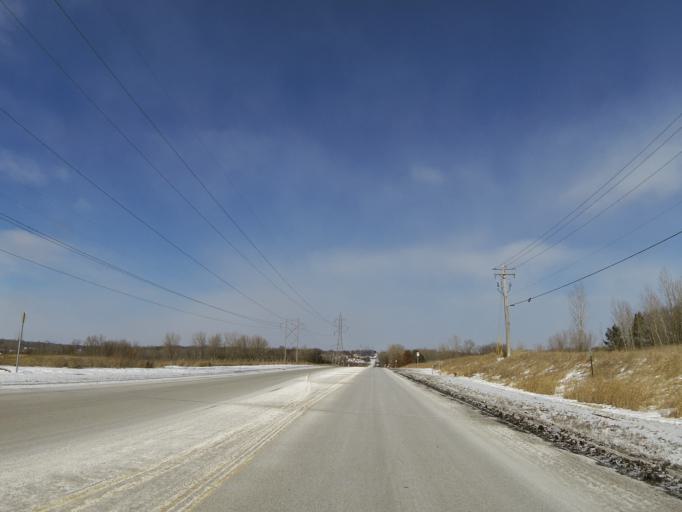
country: US
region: Minnesota
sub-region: Washington County
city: Woodbury
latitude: 44.9374
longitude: -92.9645
